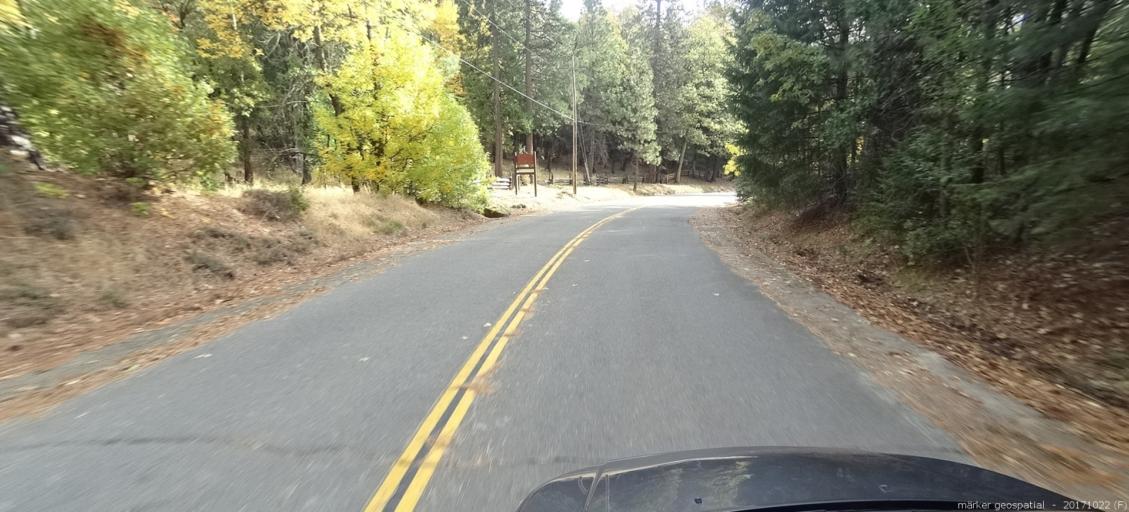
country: US
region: California
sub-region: Siskiyou County
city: Dunsmuir
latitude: 41.1492
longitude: -122.3182
